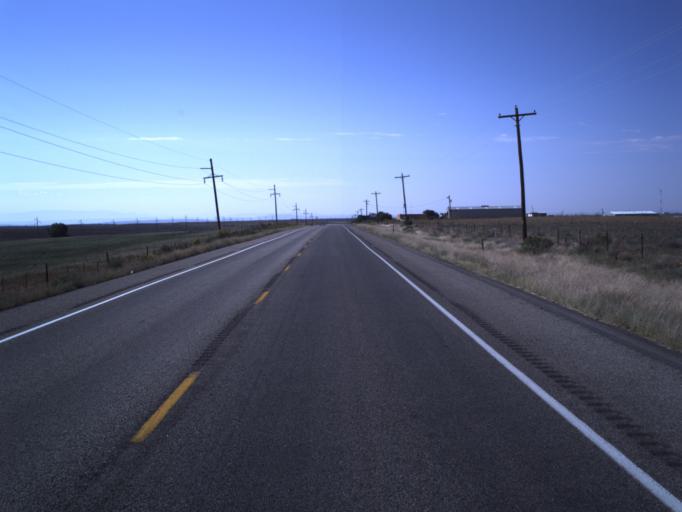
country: US
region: Utah
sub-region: San Juan County
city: Blanding
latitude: 37.5874
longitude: -109.4783
